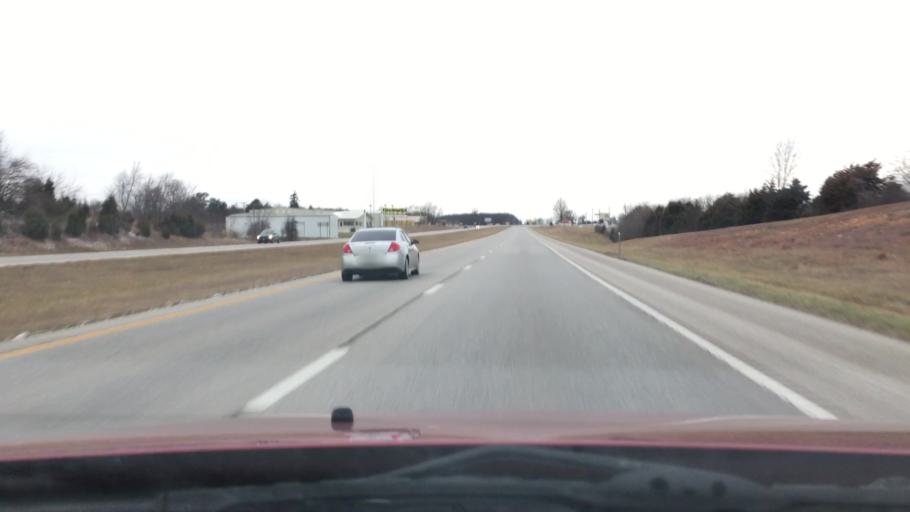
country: US
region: Missouri
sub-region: Webster County
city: Seymour
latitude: 37.1566
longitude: -92.7760
